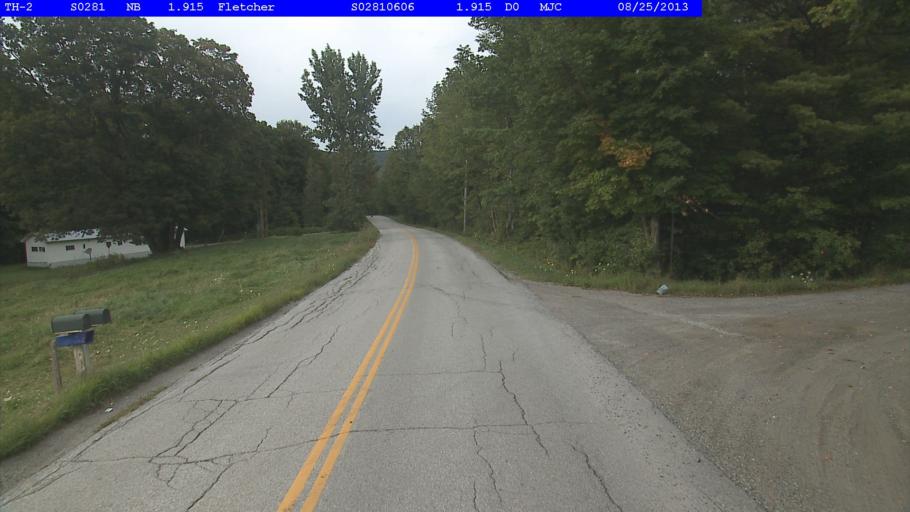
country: US
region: Vermont
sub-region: Franklin County
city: Saint Albans
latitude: 44.7019
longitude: -72.9377
